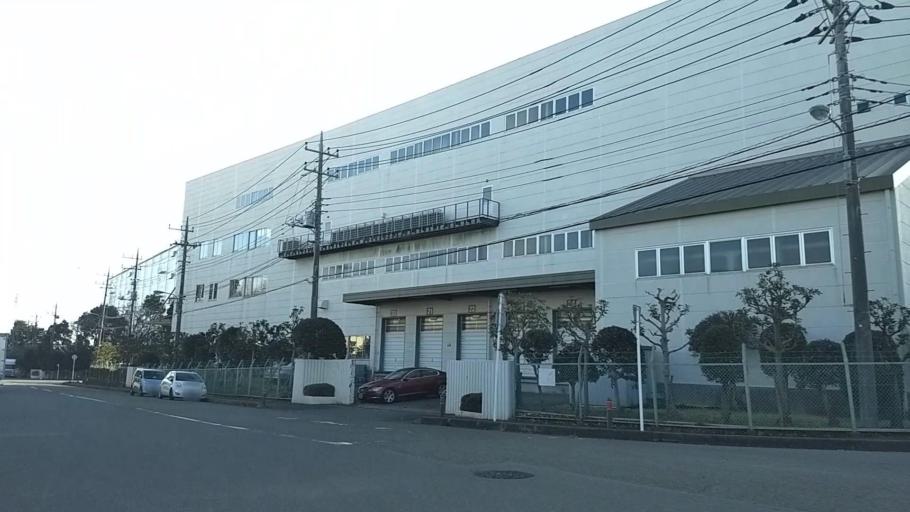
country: JP
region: Kanagawa
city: Atsugi
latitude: 35.4613
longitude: 139.3254
